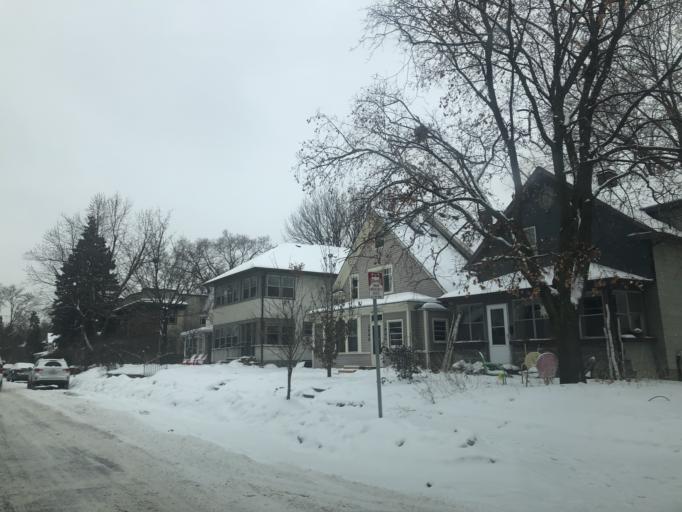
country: US
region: Minnesota
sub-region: Hennepin County
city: Richfield
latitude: 44.9322
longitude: -93.2844
